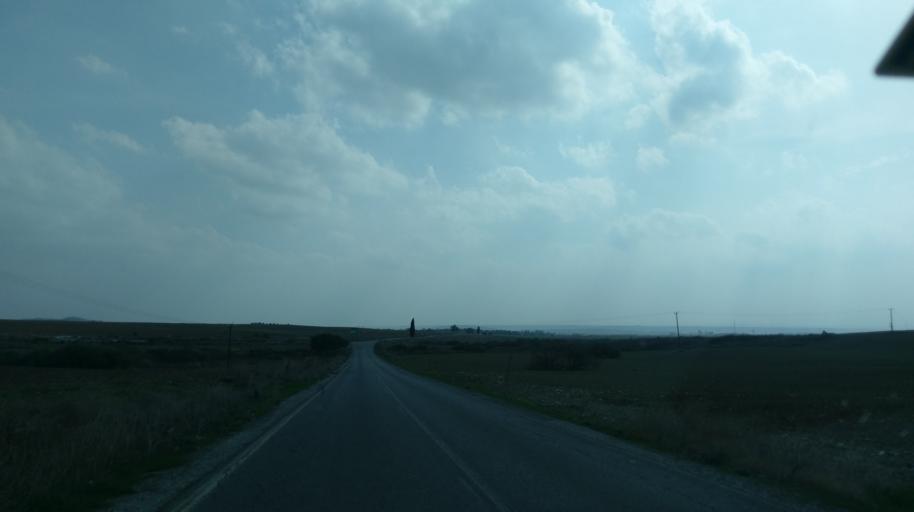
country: CY
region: Lefkosia
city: Mammari
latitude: 35.2492
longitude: 33.1509
